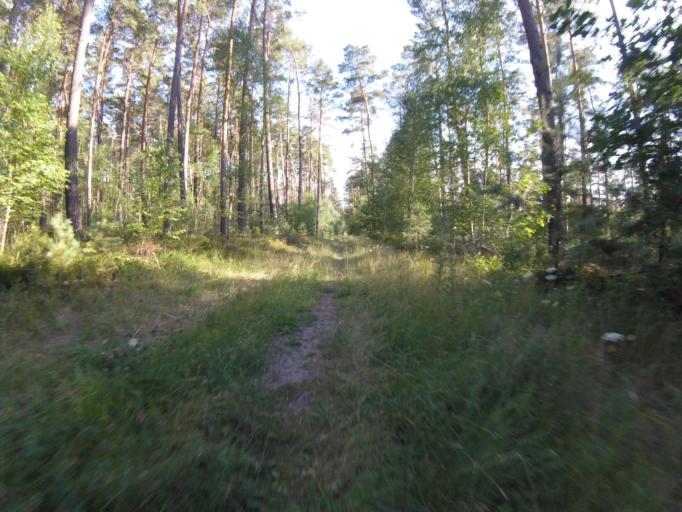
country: DE
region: Berlin
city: Schmockwitz
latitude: 52.3394
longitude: 13.7197
